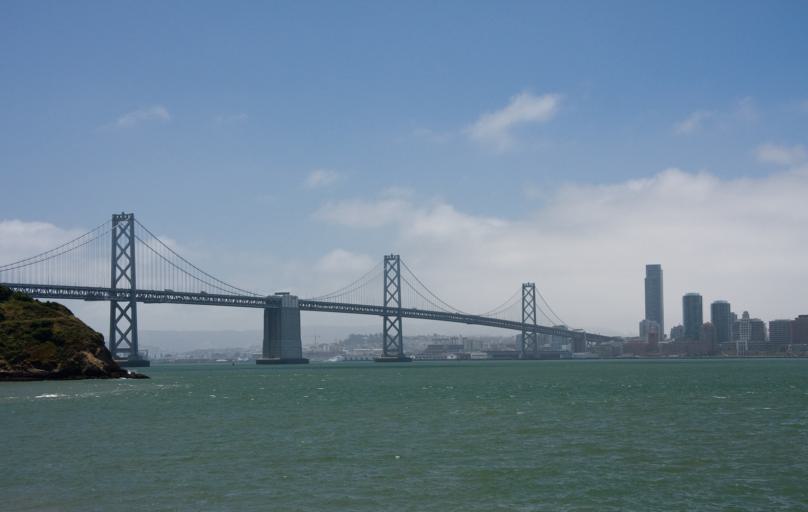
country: US
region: California
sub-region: San Francisco County
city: San Francisco
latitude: 37.8159
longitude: -122.3718
